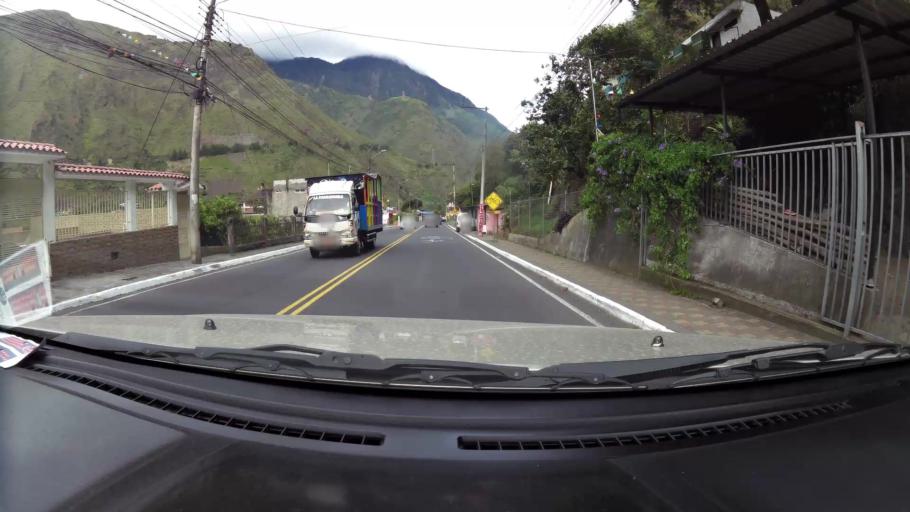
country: EC
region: Tungurahua
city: Banos
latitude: -1.3950
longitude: -78.4029
